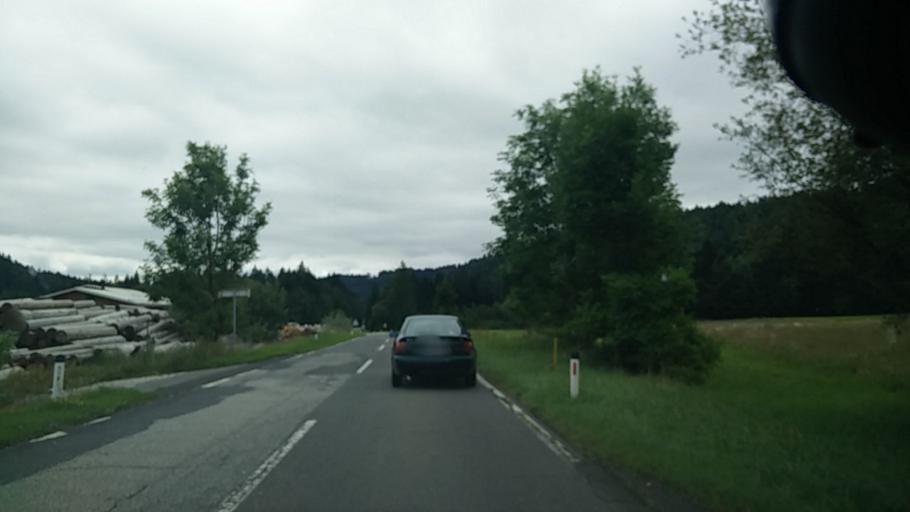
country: AT
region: Carinthia
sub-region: Politischer Bezirk Villach Land
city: Rosegg
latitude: 46.5519
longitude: 13.9936
